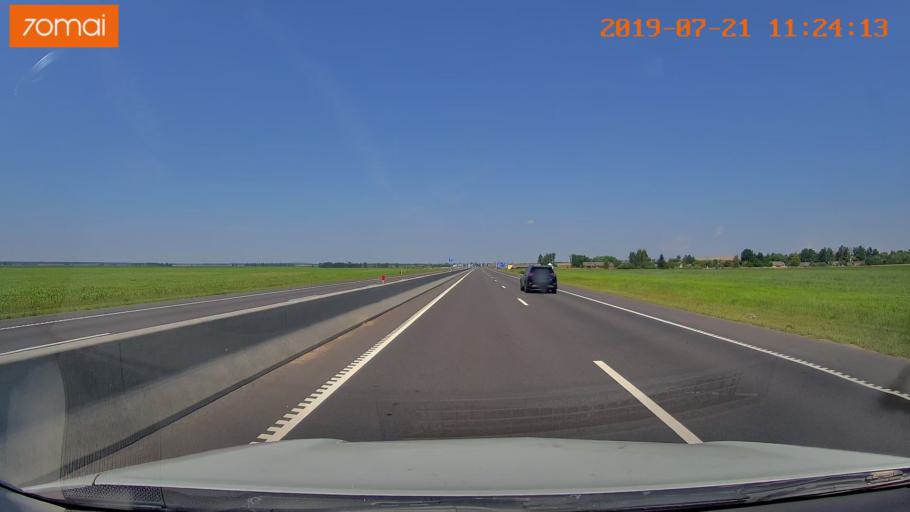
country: BY
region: Minsk
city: Valozhyn
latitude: 54.0549
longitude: 26.5488
